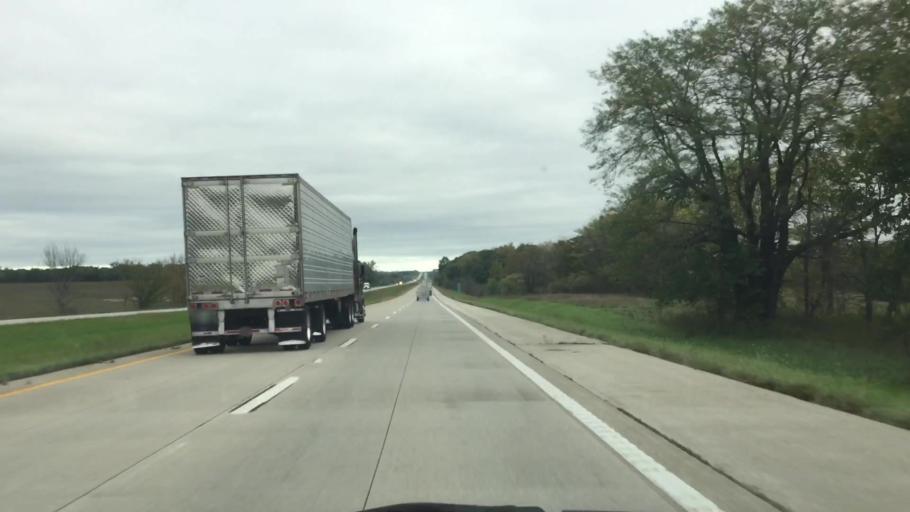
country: US
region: Missouri
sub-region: Daviess County
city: Gallatin
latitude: 40.0140
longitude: -94.0961
